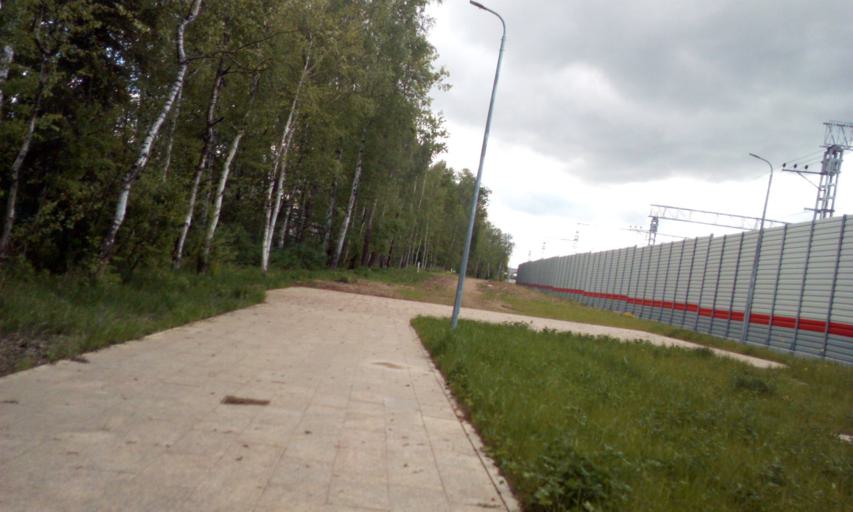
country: RU
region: Moskovskaya
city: Kokoshkino
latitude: 55.5830
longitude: 37.1343
